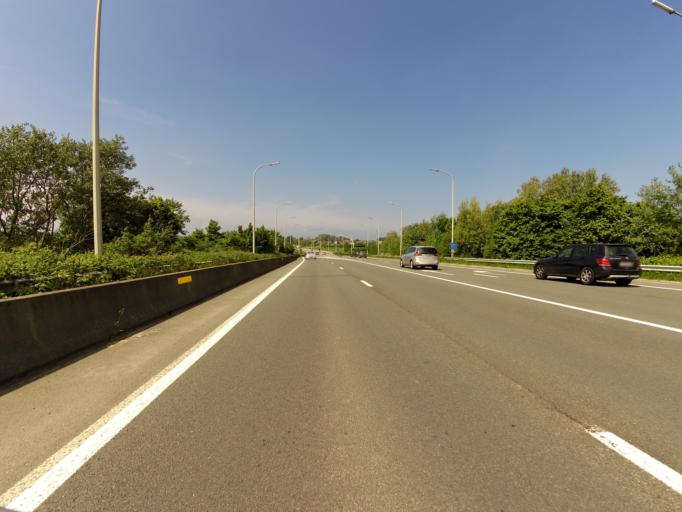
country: BE
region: Flanders
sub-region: Provincie West-Vlaanderen
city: Nieuwpoort
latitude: 51.1218
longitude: 2.7447
